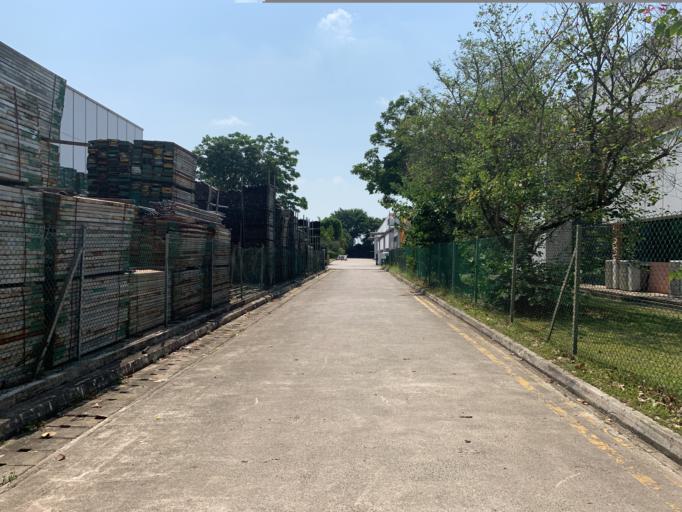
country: MY
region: Johor
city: Johor Bahru
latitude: 1.3059
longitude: 103.6291
